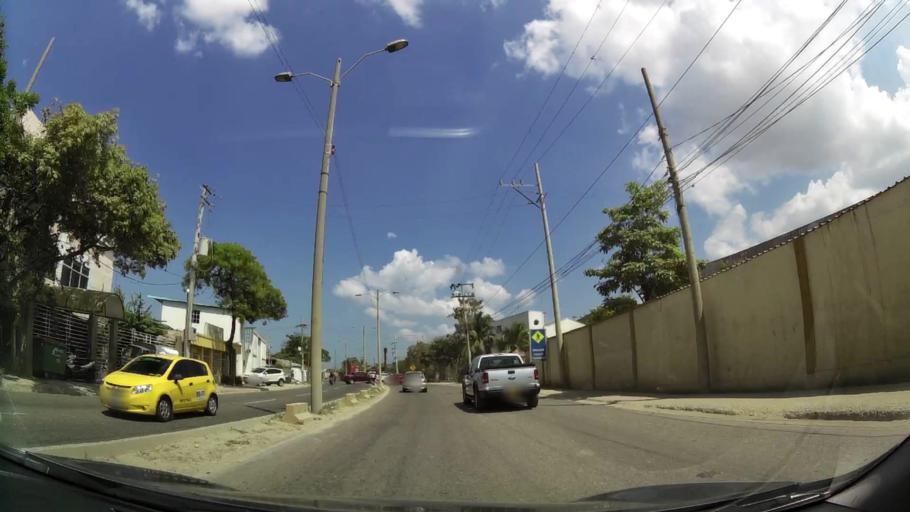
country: CO
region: Bolivar
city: Cartagena
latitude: 10.3691
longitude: -75.5067
